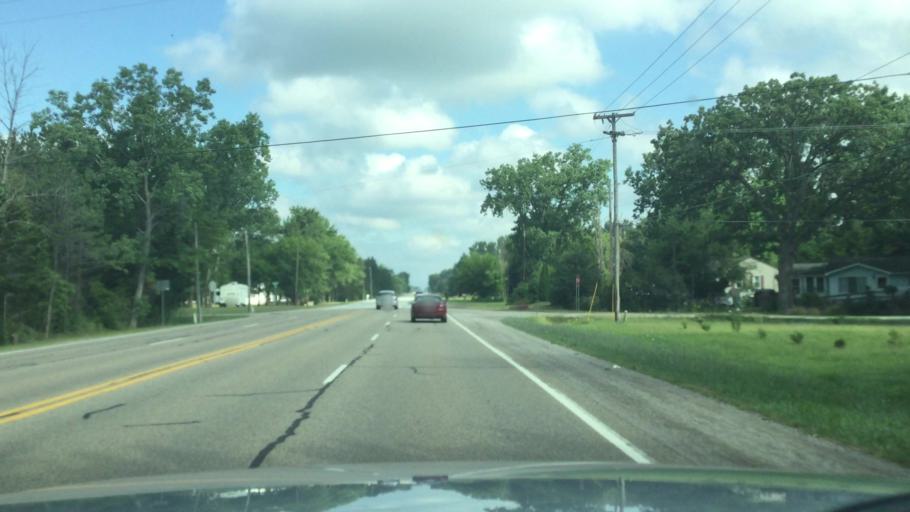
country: US
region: Michigan
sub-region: Genesee County
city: Clio
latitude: 43.2207
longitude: -83.7471
